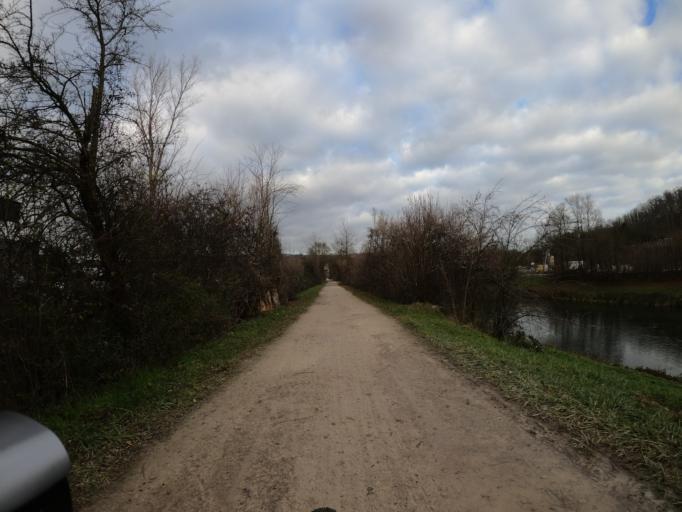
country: DE
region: Baden-Wuerttemberg
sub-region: Regierungsbezirk Stuttgart
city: Wernau
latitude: 48.7002
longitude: 9.4171
